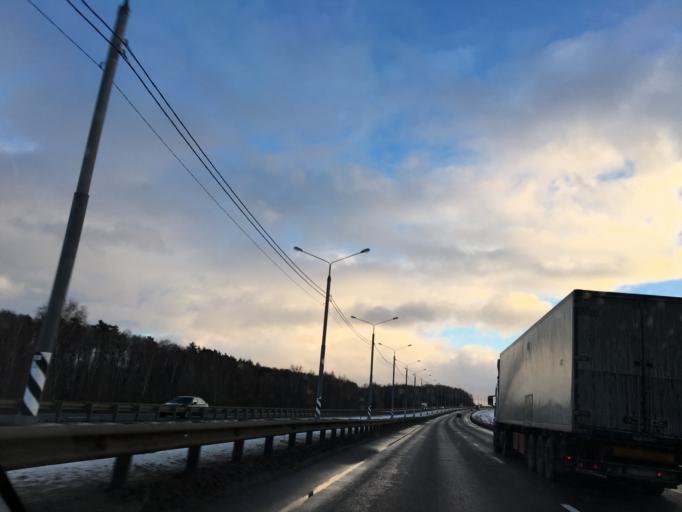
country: RU
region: Tula
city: Zaokskiy
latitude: 54.8191
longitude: 37.4753
